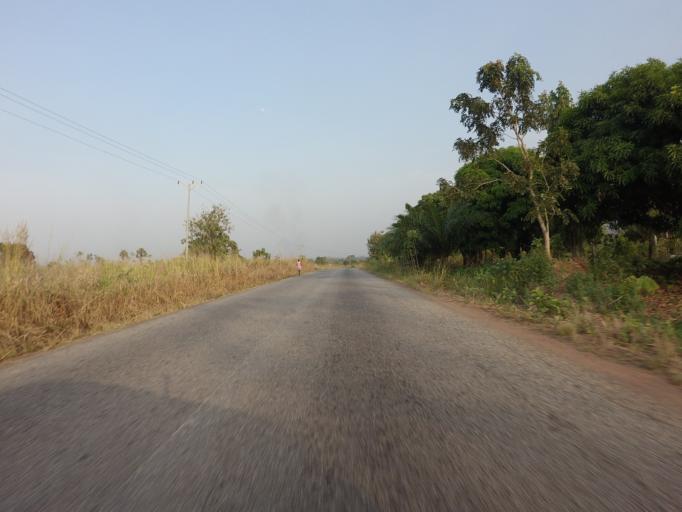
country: GH
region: Volta
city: Ho
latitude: 6.5734
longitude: 0.3587
